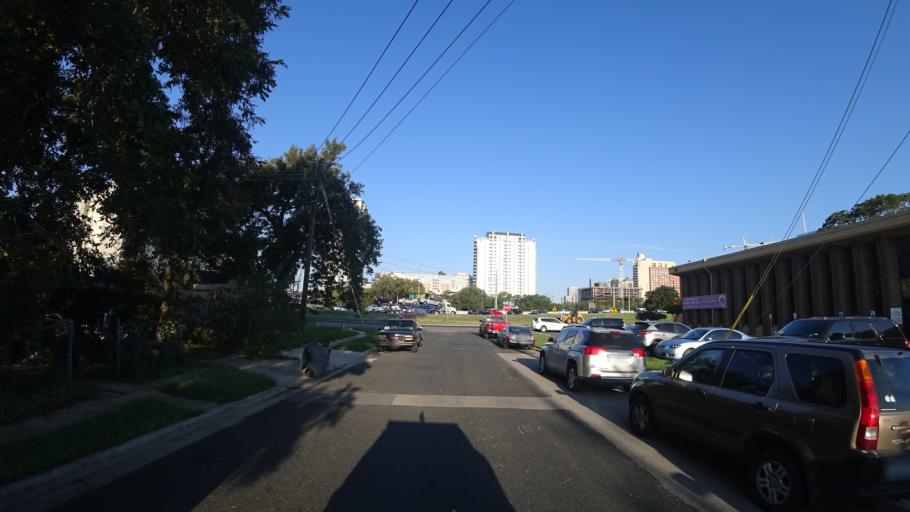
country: US
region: Texas
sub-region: Travis County
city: Austin
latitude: 30.2557
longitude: -97.7361
